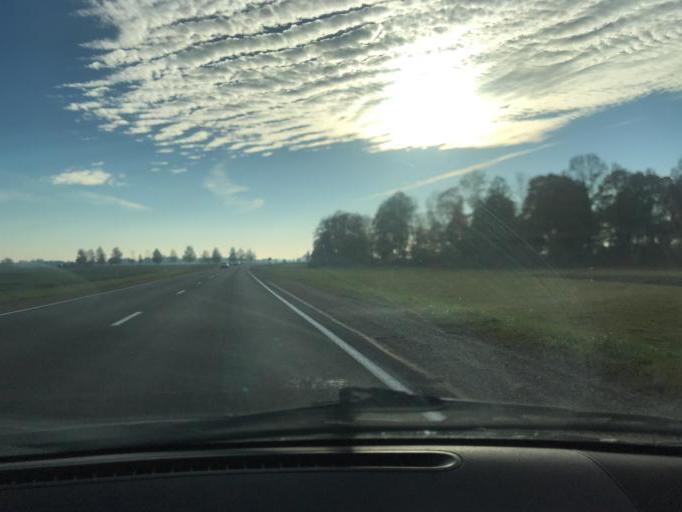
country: BY
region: Brest
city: Drahichyn
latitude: 52.2095
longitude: 25.2128
